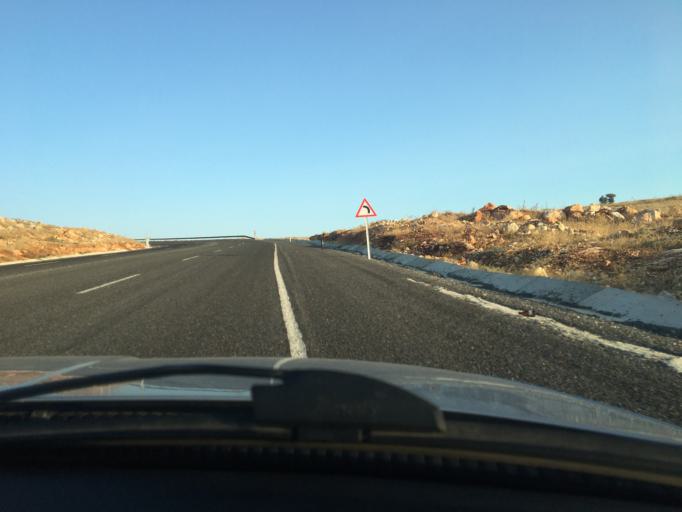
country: TR
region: Sanliurfa
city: Halfeti
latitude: 37.2389
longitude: 37.8822
